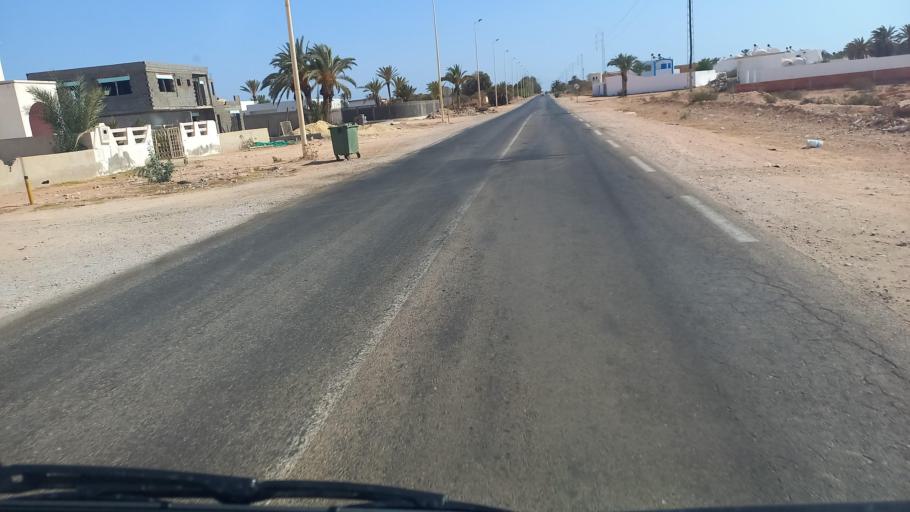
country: TN
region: Madanin
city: Midoun
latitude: 33.7639
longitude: 11.0154
